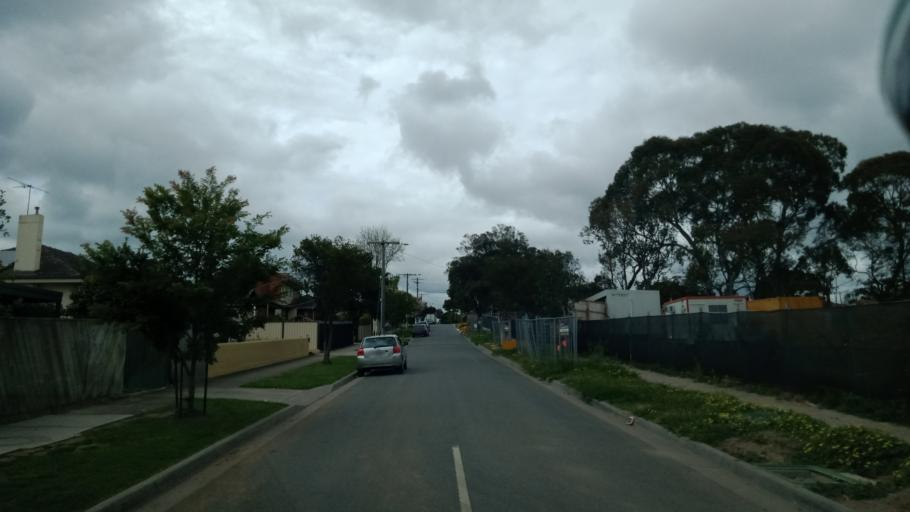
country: AU
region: Victoria
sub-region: Casey
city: Doveton
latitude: -37.9921
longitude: 145.2337
